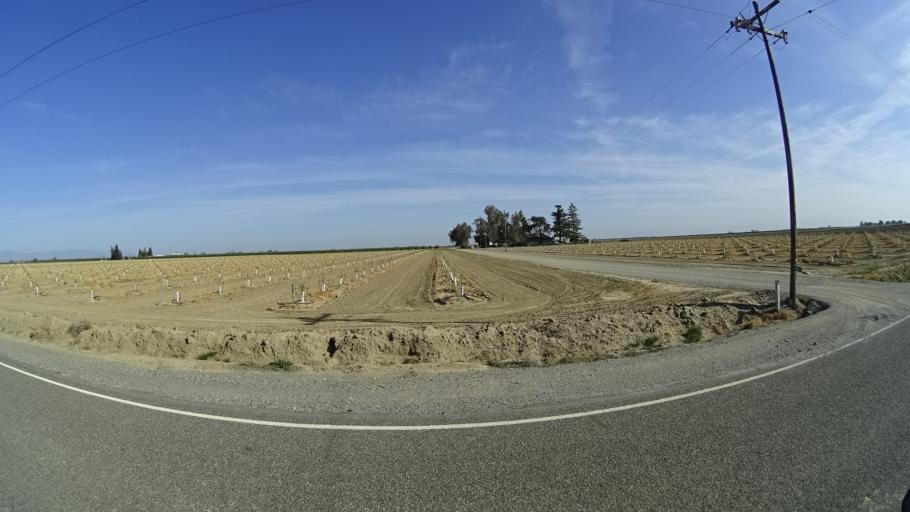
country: US
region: California
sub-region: Glenn County
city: Willows
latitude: 39.5532
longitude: -122.1466
